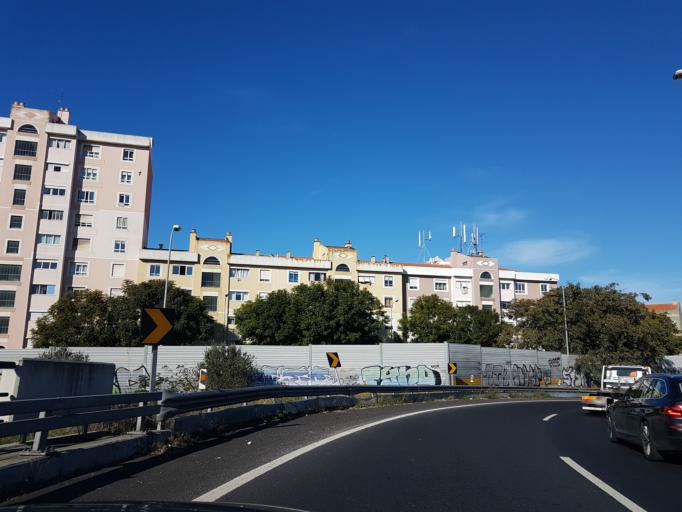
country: PT
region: Lisbon
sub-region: Amadora
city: Amadora
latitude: 38.7407
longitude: -9.2065
